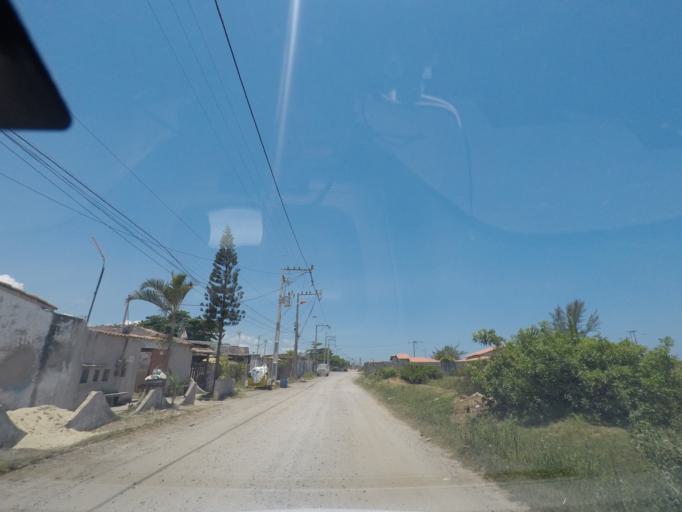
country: BR
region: Rio de Janeiro
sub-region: Niteroi
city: Niteroi
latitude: -22.9680
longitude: -42.9802
